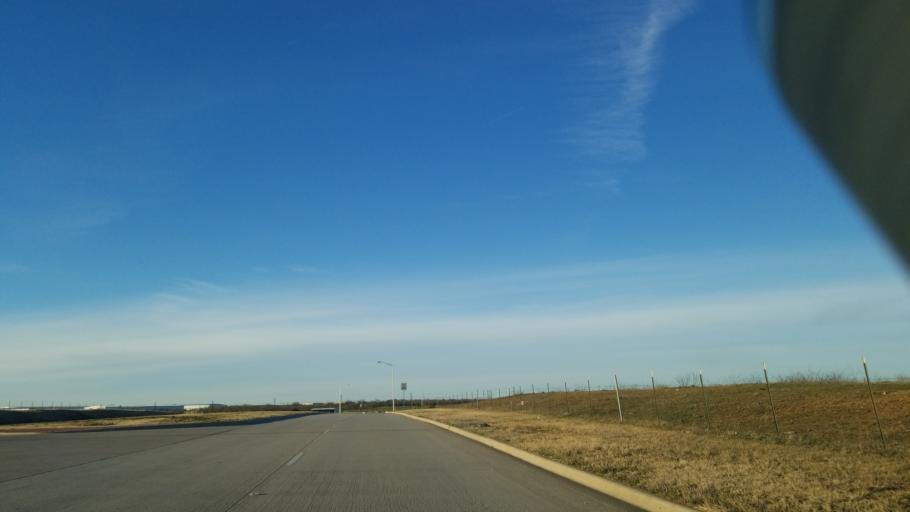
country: US
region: Texas
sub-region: Denton County
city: Denton
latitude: 33.2149
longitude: -97.1851
